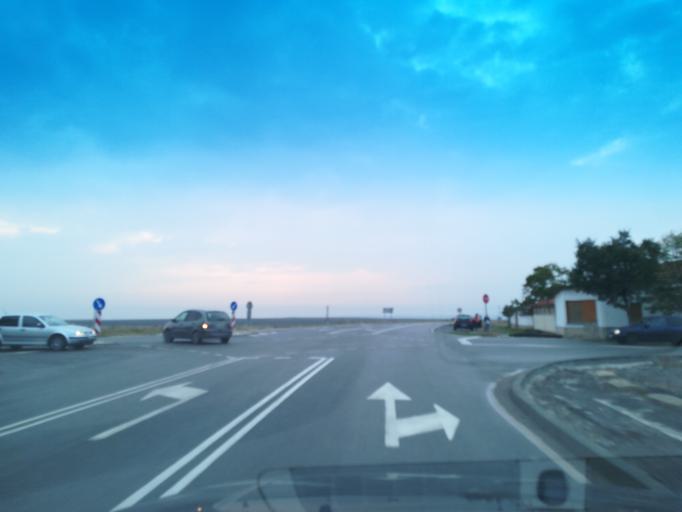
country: BG
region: Stara Zagora
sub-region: Obshtina Chirpan
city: Chirpan
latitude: 42.1886
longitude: 25.3297
